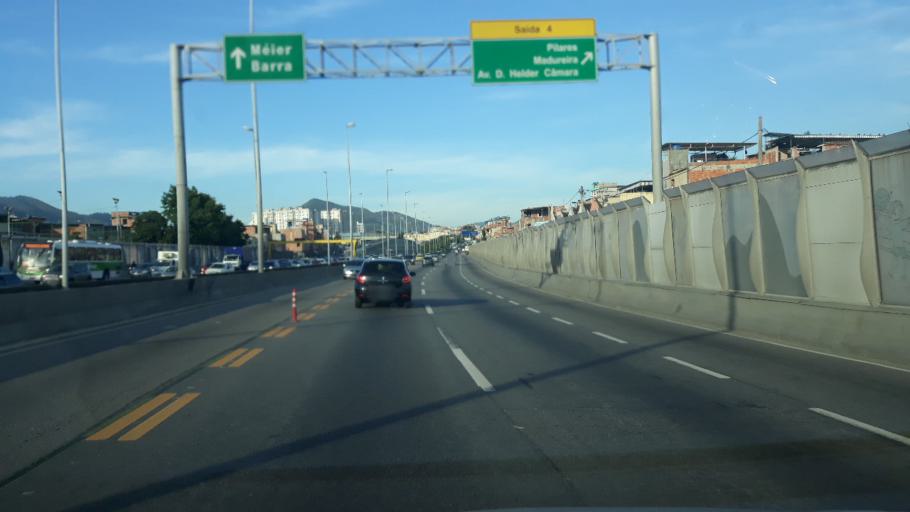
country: BR
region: Rio de Janeiro
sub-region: Rio De Janeiro
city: Rio de Janeiro
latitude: -22.8808
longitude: -43.2808
